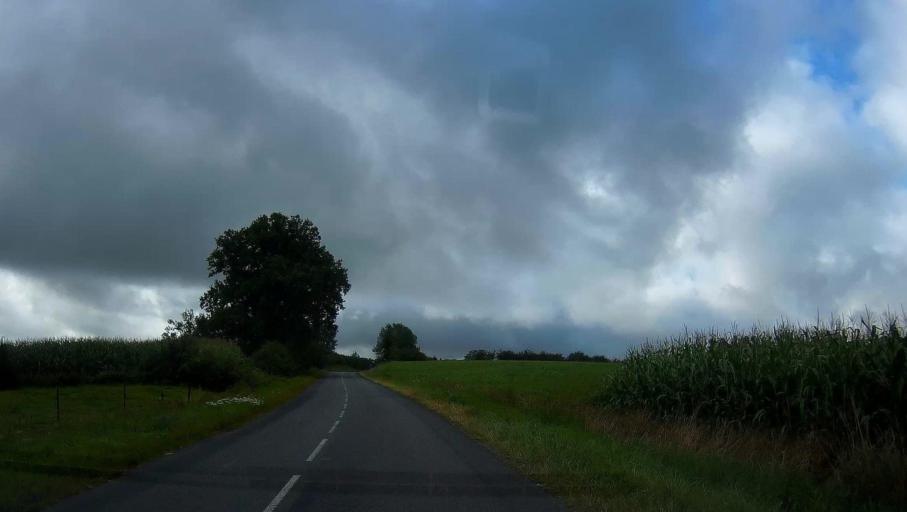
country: FR
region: Picardie
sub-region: Departement de l'Aisne
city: Rozoy-sur-Serre
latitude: 49.6831
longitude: 4.2532
